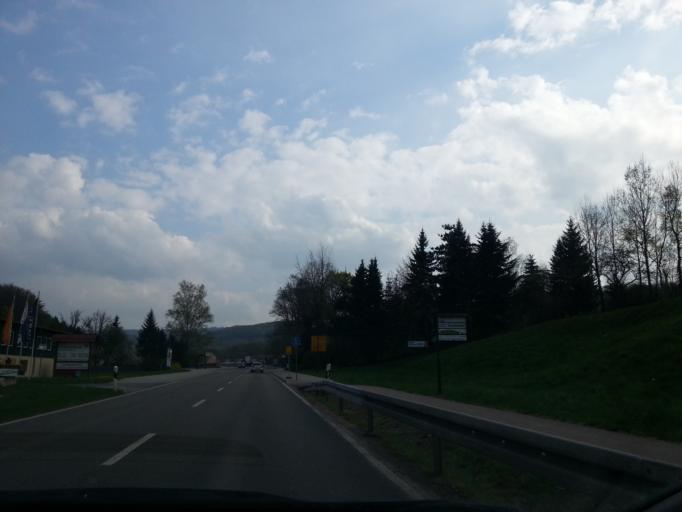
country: DE
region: Saxony
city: Schmiedeberg
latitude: 50.8514
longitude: 13.6659
